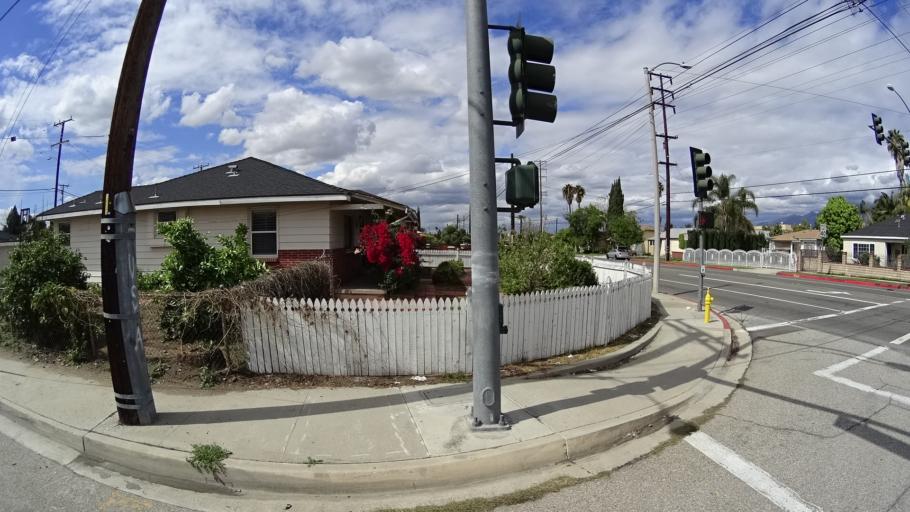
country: US
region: California
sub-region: Los Angeles County
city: Baldwin Park
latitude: 34.0920
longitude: -117.9693
